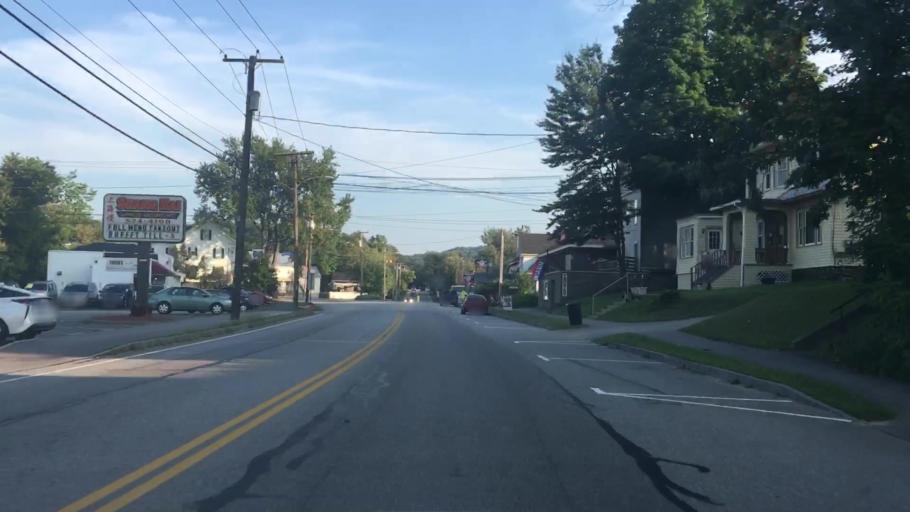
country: US
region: New Hampshire
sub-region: Belknap County
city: Laconia
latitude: 43.5229
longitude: -71.4669
